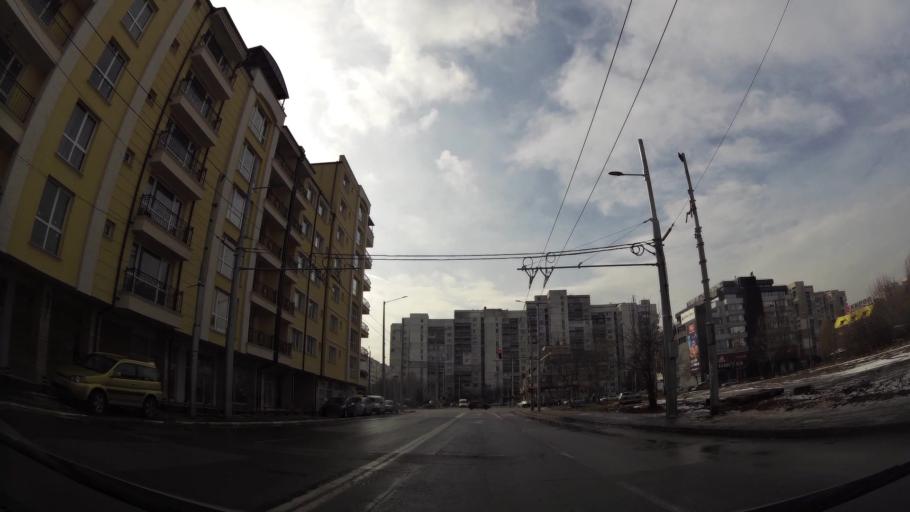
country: BG
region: Sofia-Capital
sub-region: Stolichna Obshtina
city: Sofia
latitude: 42.7143
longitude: 23.2665
